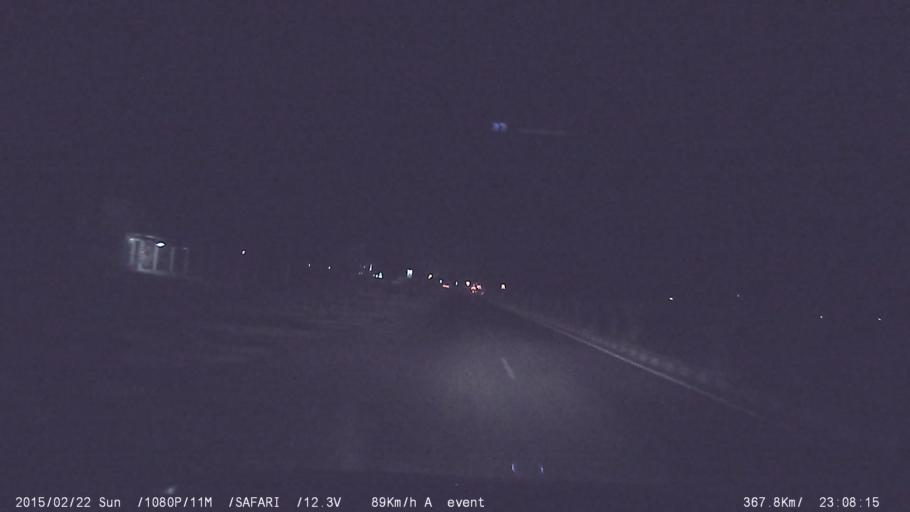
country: IN
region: Tamil Nadu
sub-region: Namakkal
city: Rasipuram
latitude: 11.4503
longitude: 78.1588
